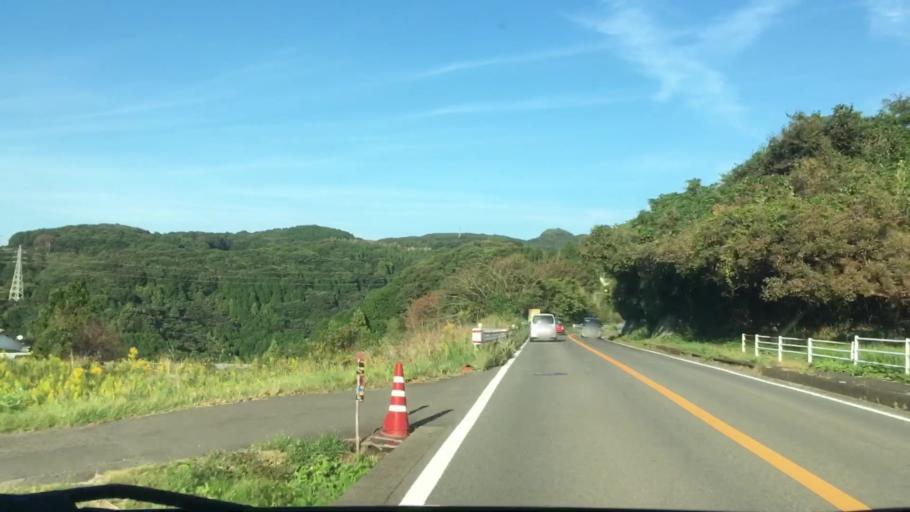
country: JP
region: Nagasaki
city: Sasebo
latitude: 33.0383
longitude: 129.6704
